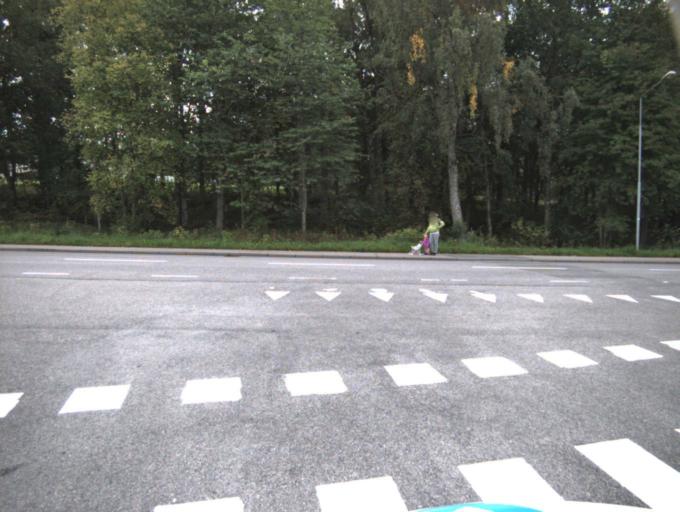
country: SE
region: Vaestra Goetaland
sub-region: Ulricehamns Kommun
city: Ulricehamn
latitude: 57.8035
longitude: 13.4338
